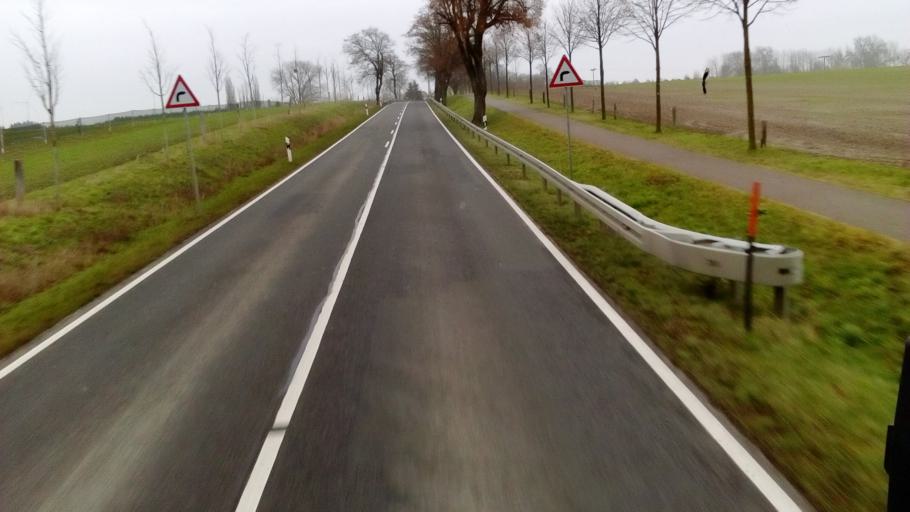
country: DE
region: Mecklenburg-Vorpommern
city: Strasburg
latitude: 53.5015
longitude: 13.7693
